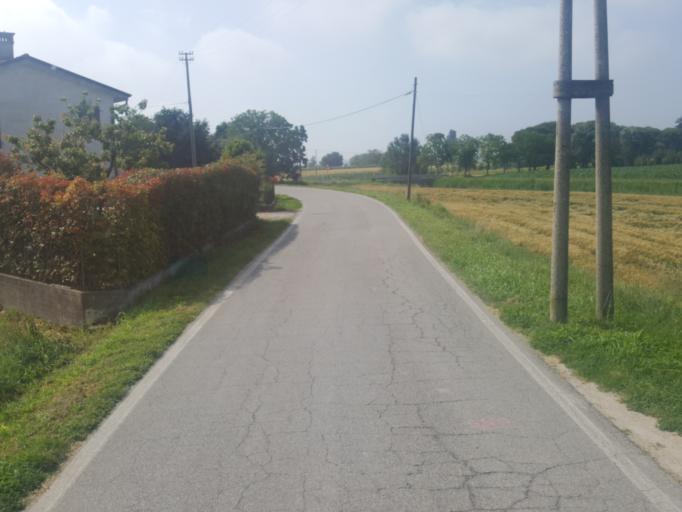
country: IT
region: Veneto
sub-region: Provincia di Rovigo
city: Canaro
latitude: 44.9377
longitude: 11.6487
